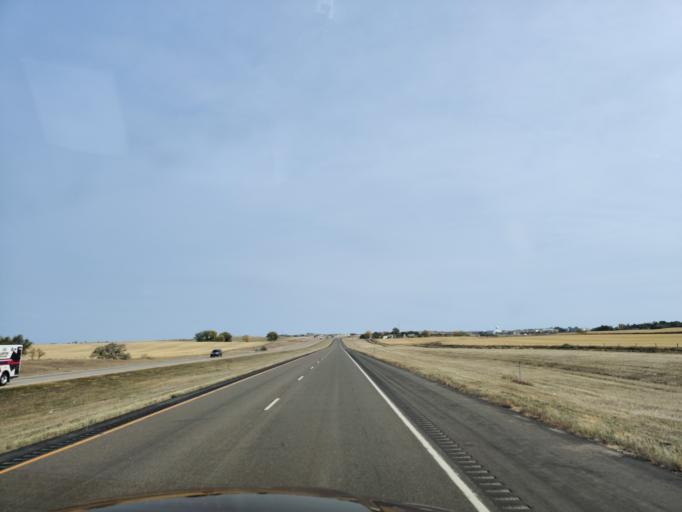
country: US
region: North Dakota
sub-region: Stark County
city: Dickinson
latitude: 46.8936
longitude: -102.7612
